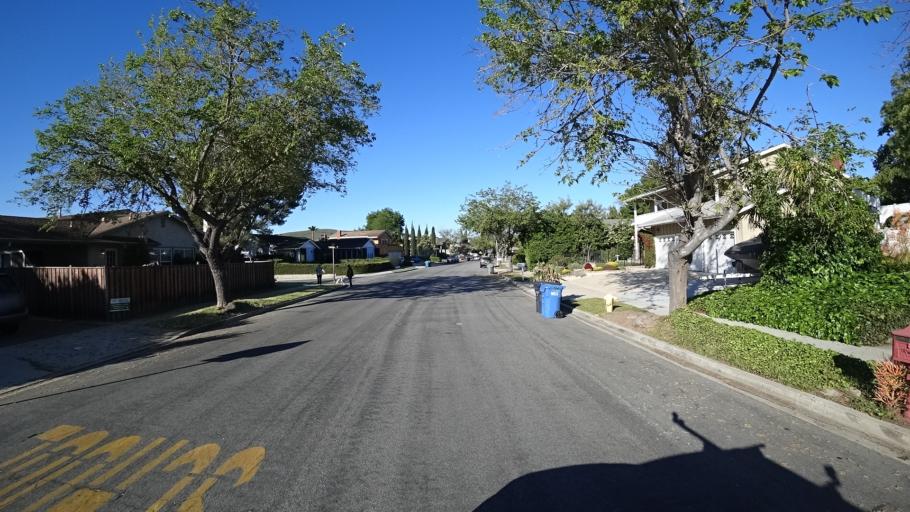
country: US
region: California
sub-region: Ventura County
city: Casa Conejo
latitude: 34.2159
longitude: -118.8947
